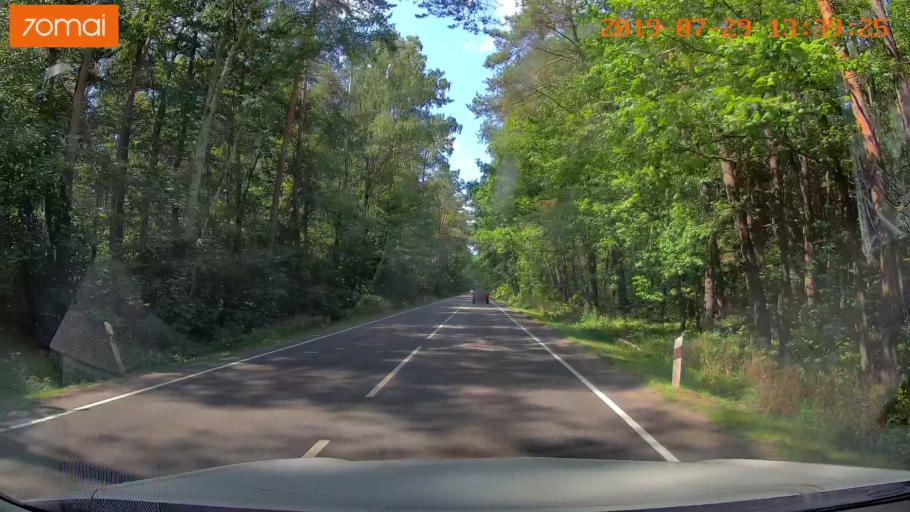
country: RU
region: Kaliningrad
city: Svetlyy
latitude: 54.7239
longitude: 20.1537
